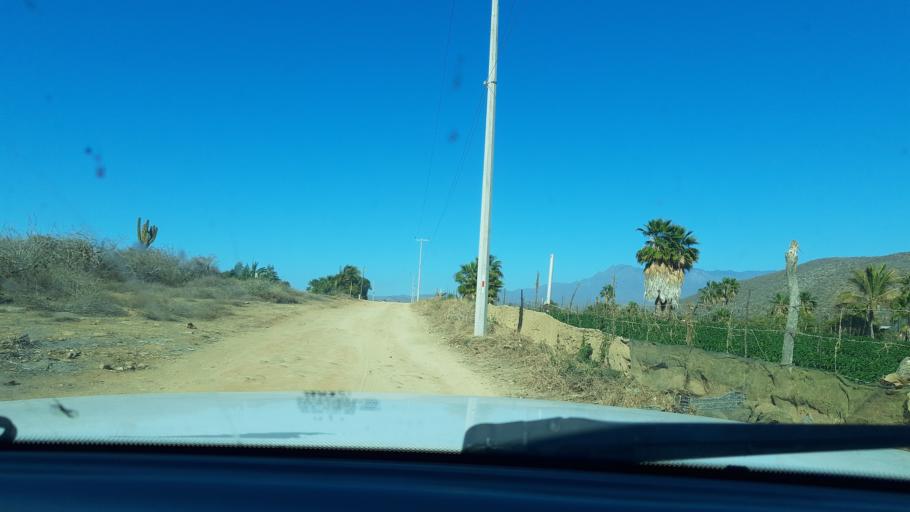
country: MX
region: Baja California Sur
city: Todos Santos
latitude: 23.4728
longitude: -110.2183
